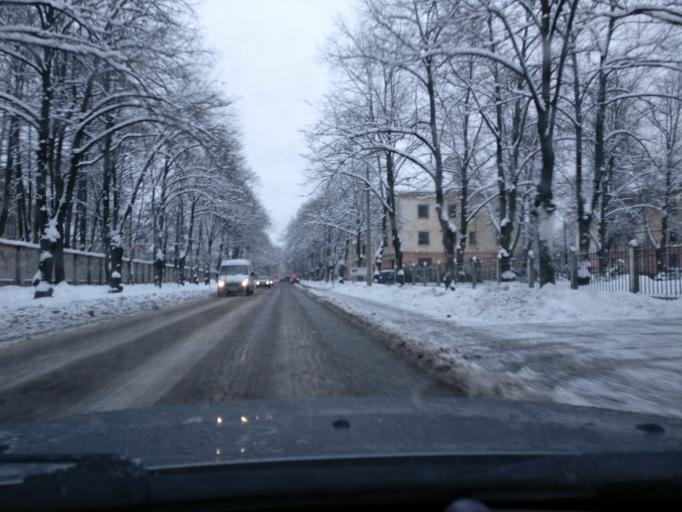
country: LV
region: Marupe
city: Marupe
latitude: 56.9307
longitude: 24.0681
